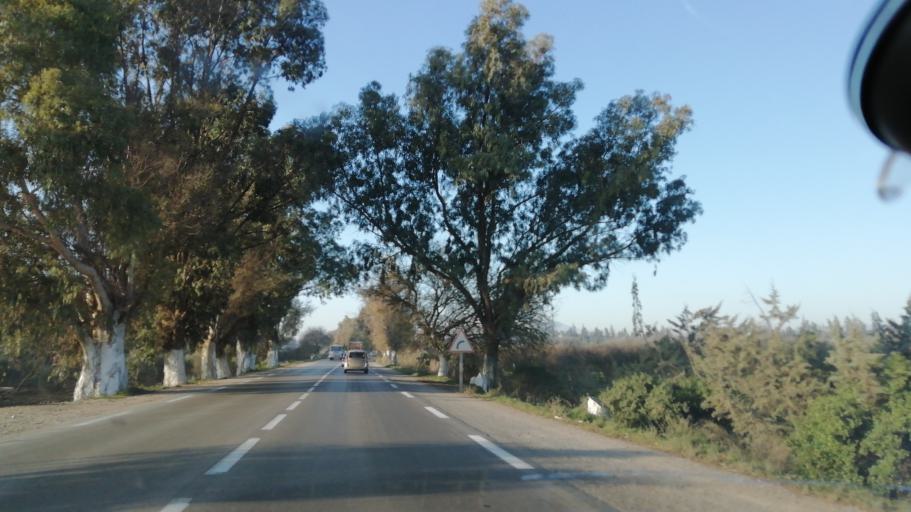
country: DZ
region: Tlemcen
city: Remchi
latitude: 35.0735
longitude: -1.4562
